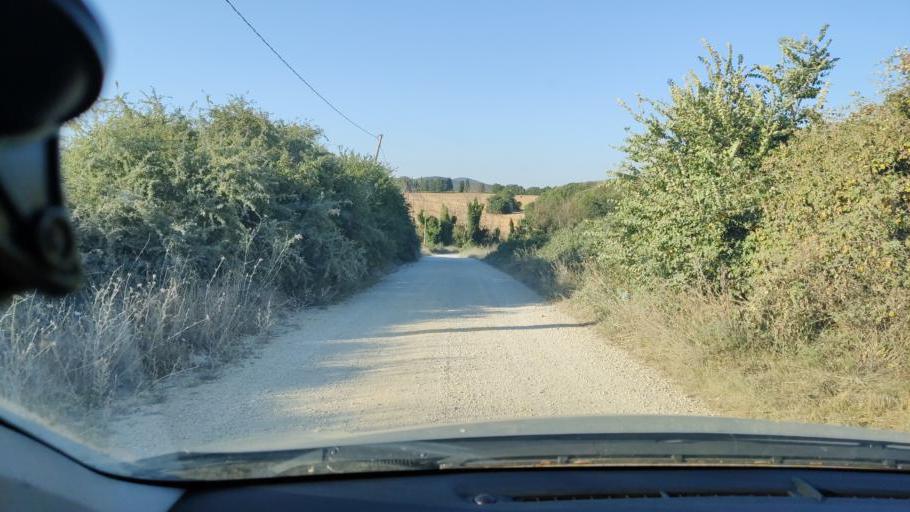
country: IT
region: Umbria
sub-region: Provincia di Terni
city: Giove
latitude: 42.5388
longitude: 12.3637
